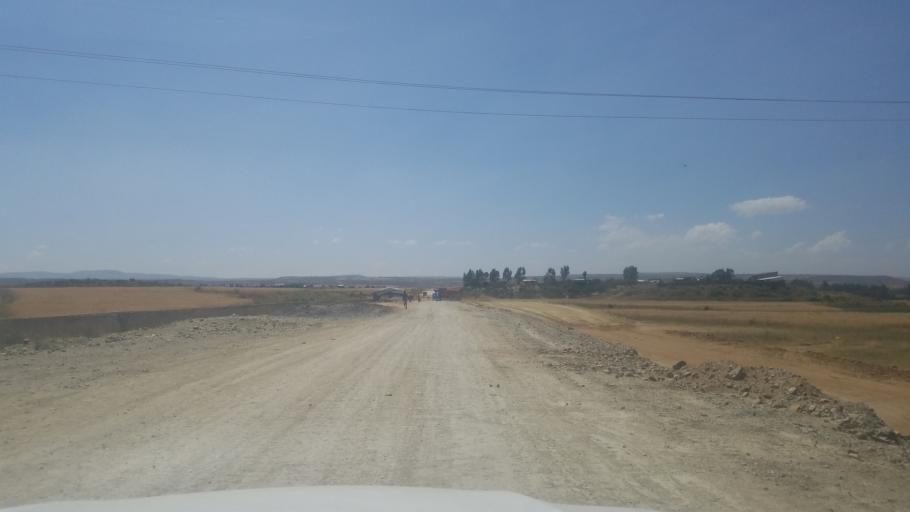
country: ET
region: Tigray
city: Mekele
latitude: 13.7650
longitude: 39.5904
